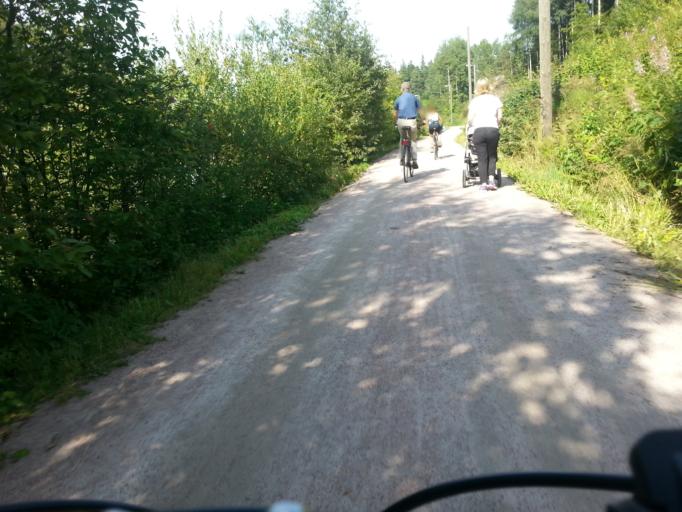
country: FI
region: Uusimaa
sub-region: Helsinki
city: Helsinki
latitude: 60.2233
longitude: 24.9830
